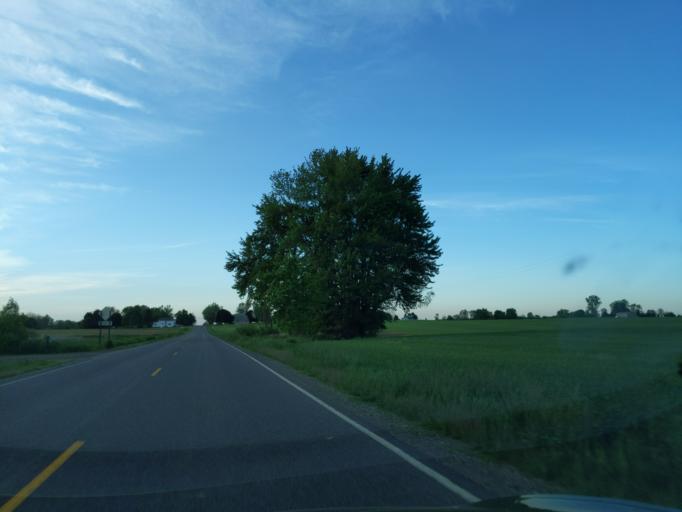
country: US
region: Michigan
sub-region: Ingham County
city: Williamston
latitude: 42.5788
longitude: -84.2985
